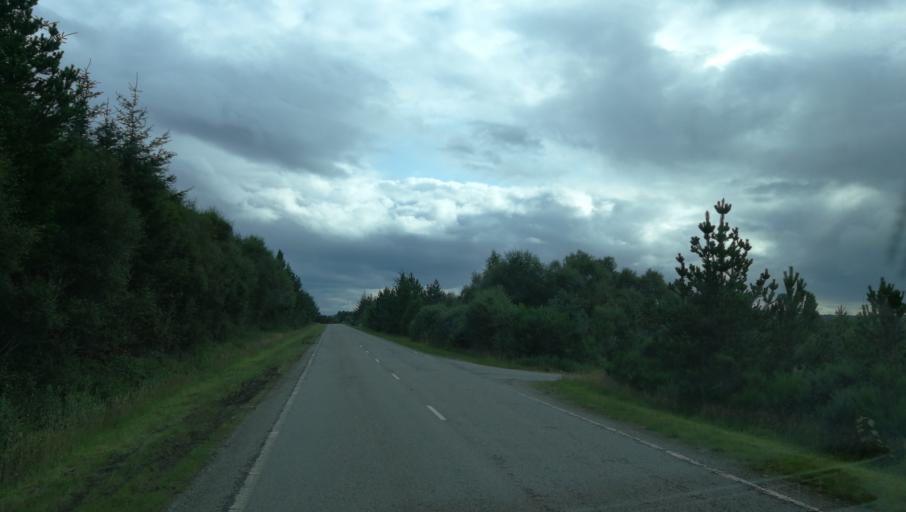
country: GB
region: Scotland
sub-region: Highland
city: Alness
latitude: 57.9960
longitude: -4.4028
